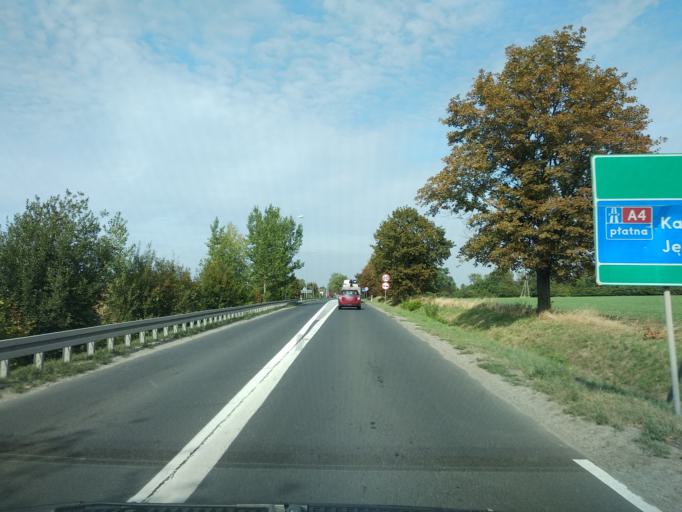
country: PL
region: Lower Silesian Voivodeship
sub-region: Powiat wroclawski
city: Zorawina
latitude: 50.9679
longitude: 17.0709
